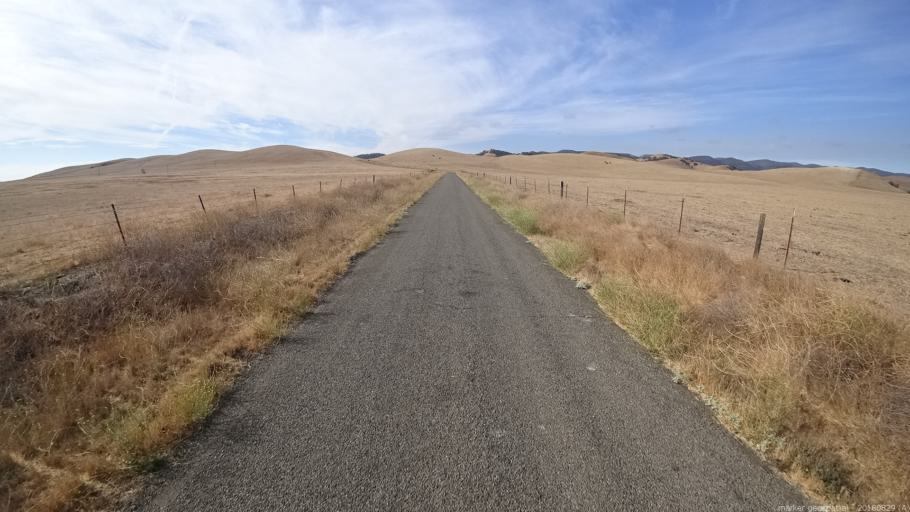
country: US
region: California
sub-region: Monterey County
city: King City
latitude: 36.0545
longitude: -120.9792
